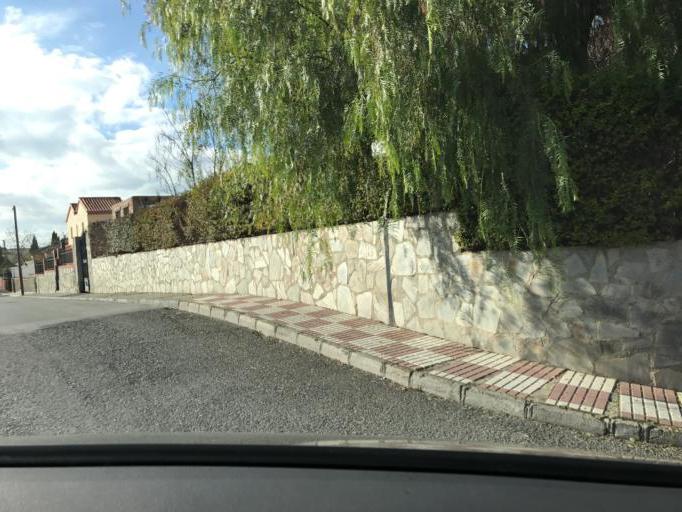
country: ES
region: Andalusia
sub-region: Provincia de Granada
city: Otura
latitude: 37.0873
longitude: -3.6290
